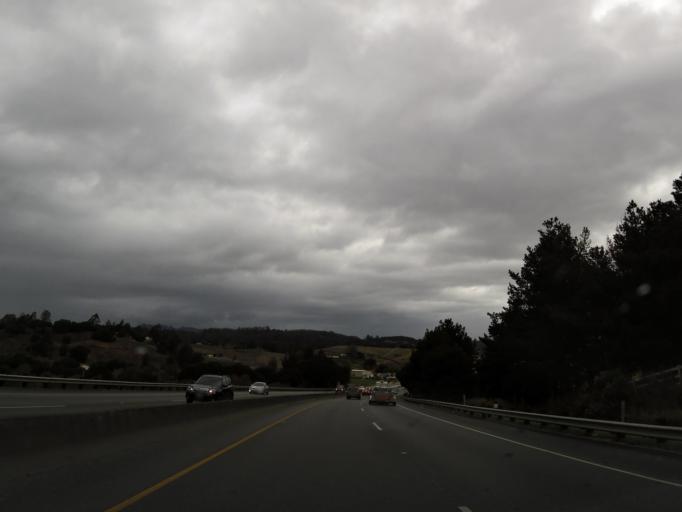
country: US
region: California
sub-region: San Benito County
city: Aromas
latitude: 36.8510
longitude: -121.6359
